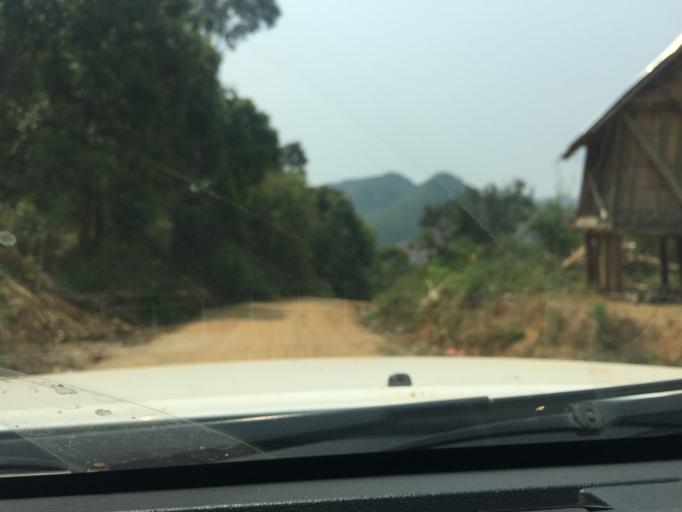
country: LA
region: Loungnamtha
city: Muang Nale
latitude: 20.6314
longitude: 101.6485
